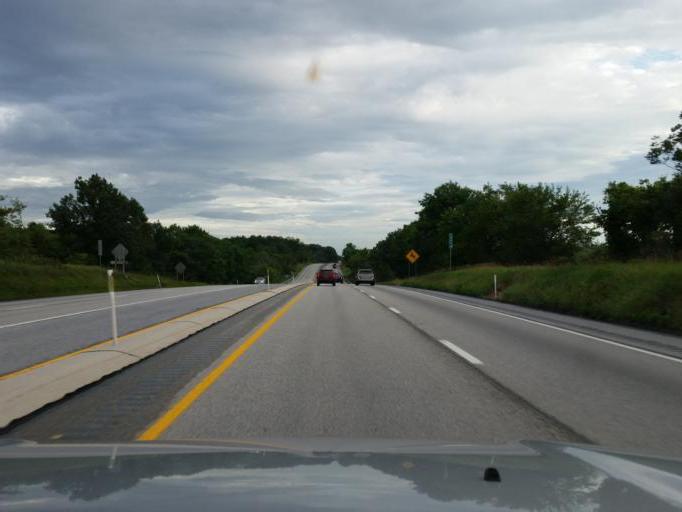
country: US
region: Pennsylvania
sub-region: York County
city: Dillsburg
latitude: 40.0878
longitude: -77.0481
